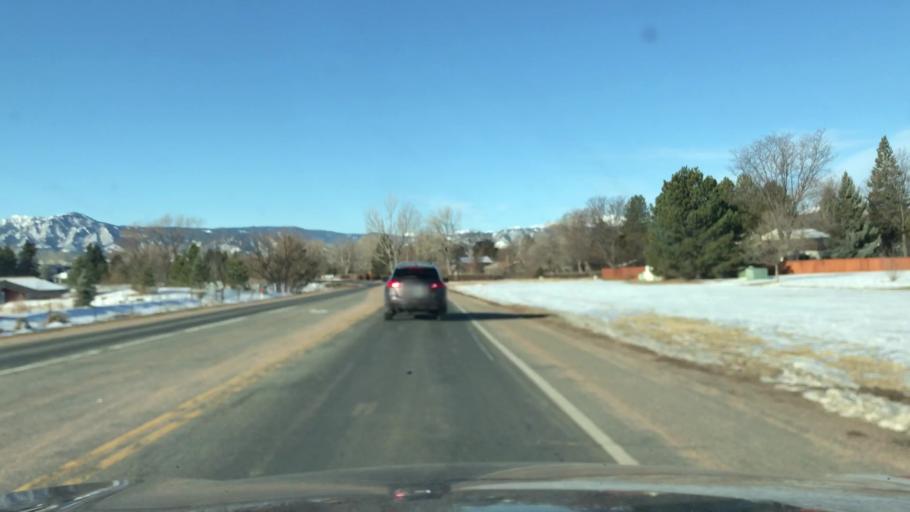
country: US
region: Colorado
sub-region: Boulder County
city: Gunbarrel
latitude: 40.0528
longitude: -105.1819
